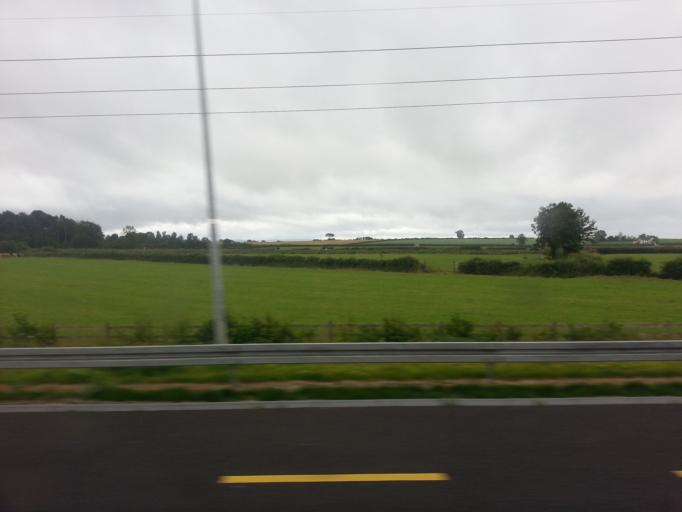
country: IE
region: Leinster
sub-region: Kilkenny
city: Kilkenny
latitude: 52.6364
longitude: -7.1598
